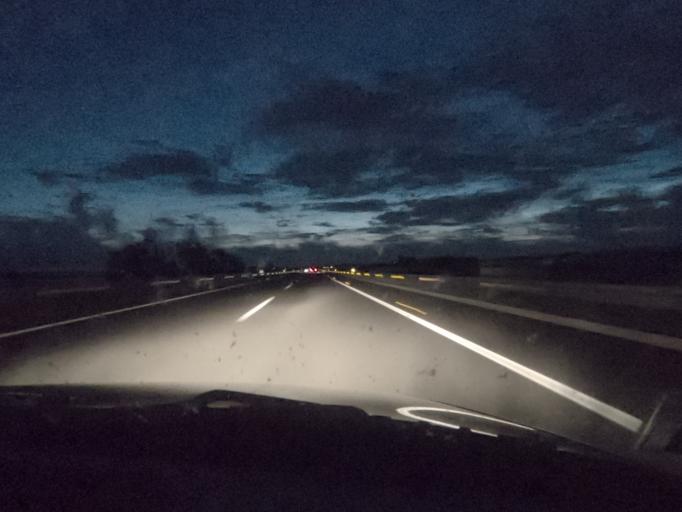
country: ES
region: Extremadura
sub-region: Provincia de Caceres
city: Morcillo
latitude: 39.9812
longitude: -6.3956
